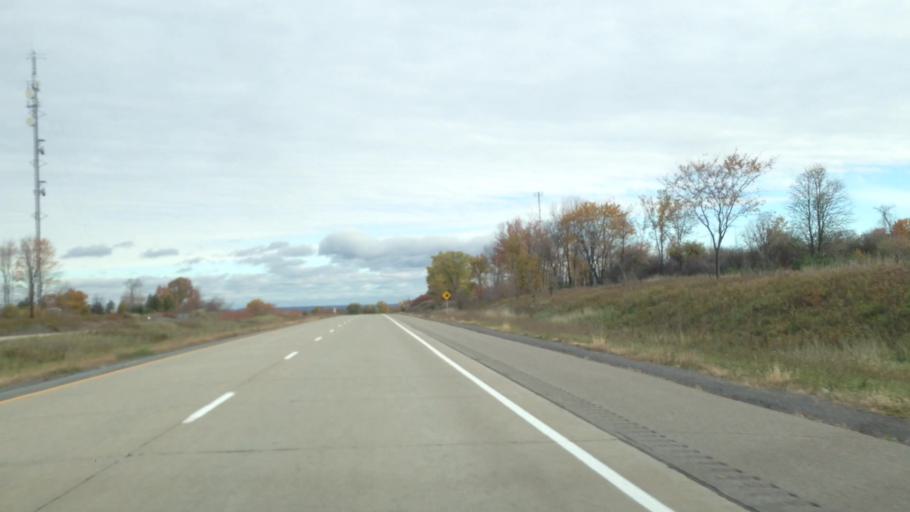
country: CA
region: Ontario
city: Hawkesbury
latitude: 45.5584
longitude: -74.5144
